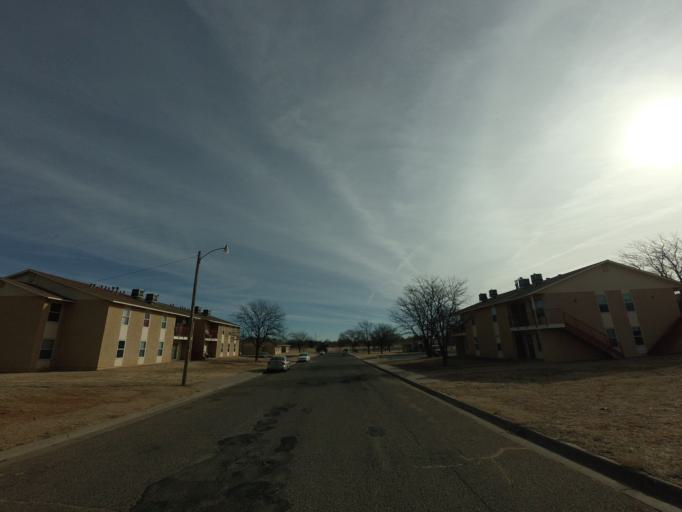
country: US
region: New Mexico
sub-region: Curry County
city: Clovis
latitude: 34.4128
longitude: -103.2220
